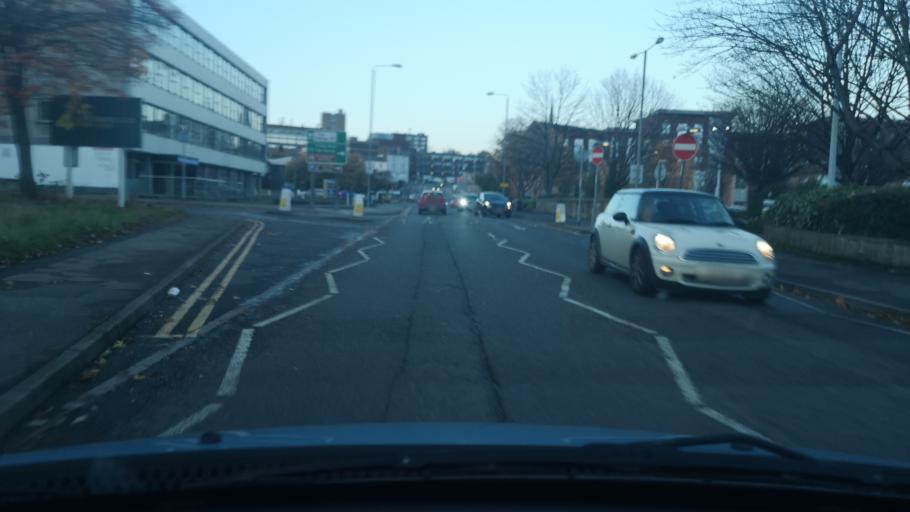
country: GB
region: England
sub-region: City and Borough of Wakefield
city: Wakefield
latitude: 53.6780
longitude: -1.5004
